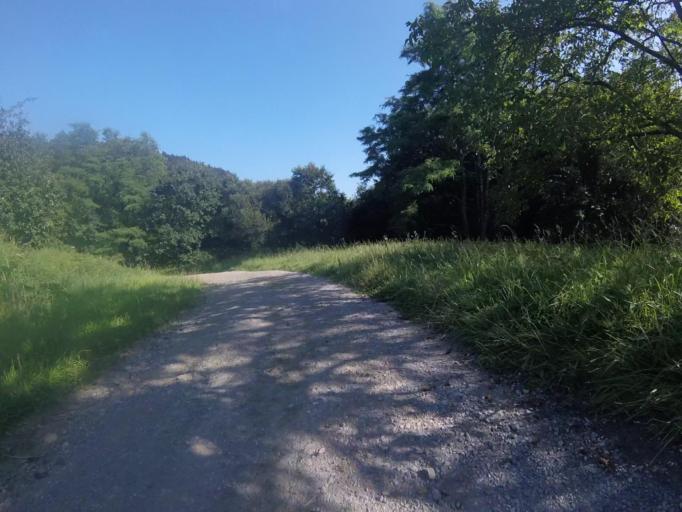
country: ES
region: Basque Country
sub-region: Provincia de Guipuzcoa
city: Astigarraga
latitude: 43.2631
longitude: -1.9376
